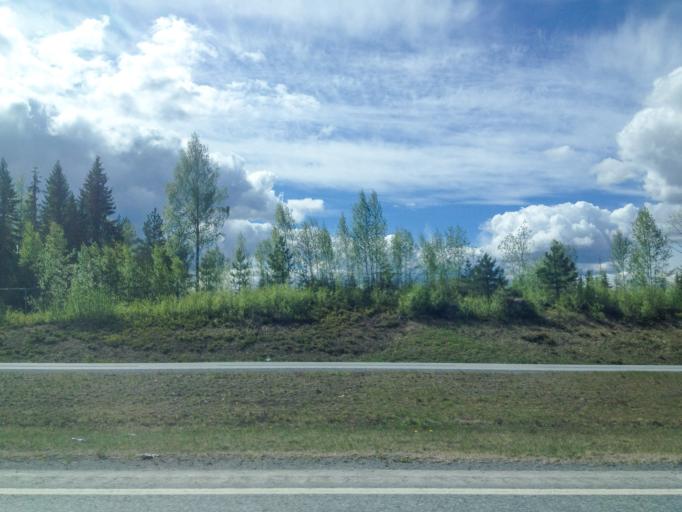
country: FI
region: Pirkanmaa
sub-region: Etelae-Pirkanmaa
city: Viiala
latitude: 61.2598
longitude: 23.8334
